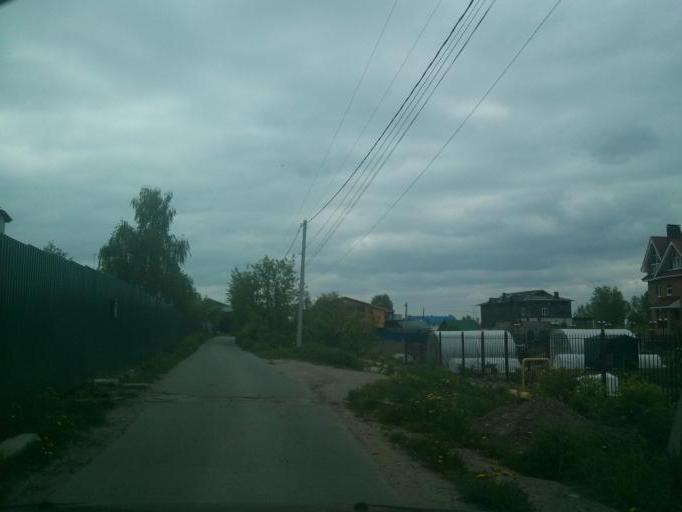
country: RU
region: Nizjnij Novgorod
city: Afonino
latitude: 56.2989
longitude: 44.1000
